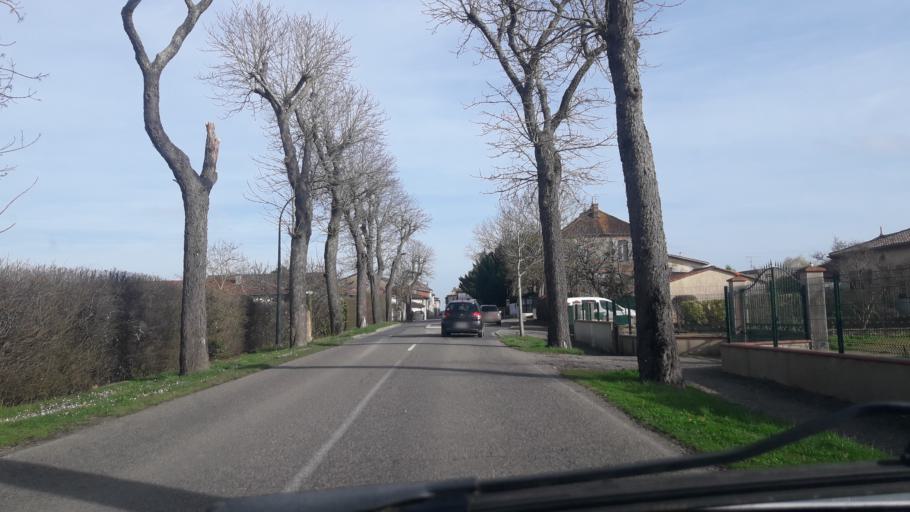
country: FR
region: Midi-Pyrenees
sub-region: Departement du Gers
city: Gimont
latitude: 43.7228
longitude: 0.9738
